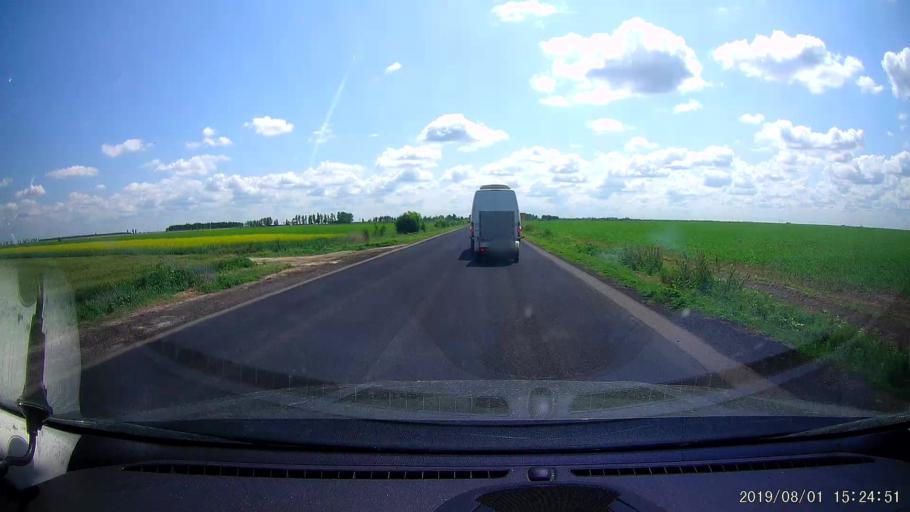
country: RO
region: Braila
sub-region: Comuna Viziru
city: Lanurile
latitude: 45.0290
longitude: 27.7440
